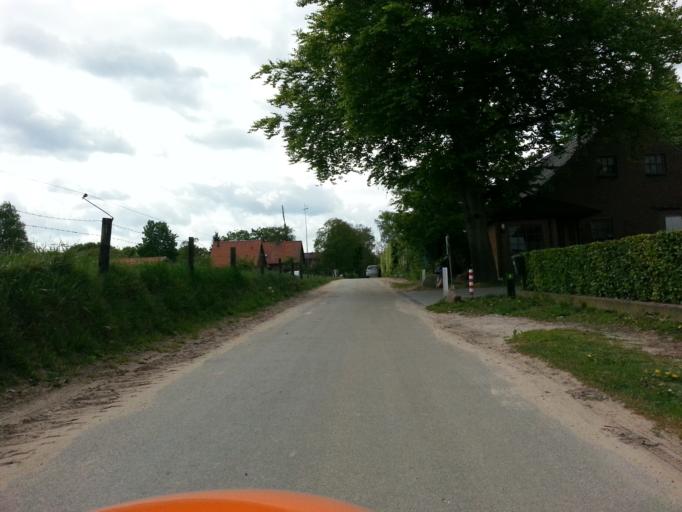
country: NL
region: Gelderland
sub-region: Gemeente Ede
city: Ede
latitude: 52.0633
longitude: 5.6475
